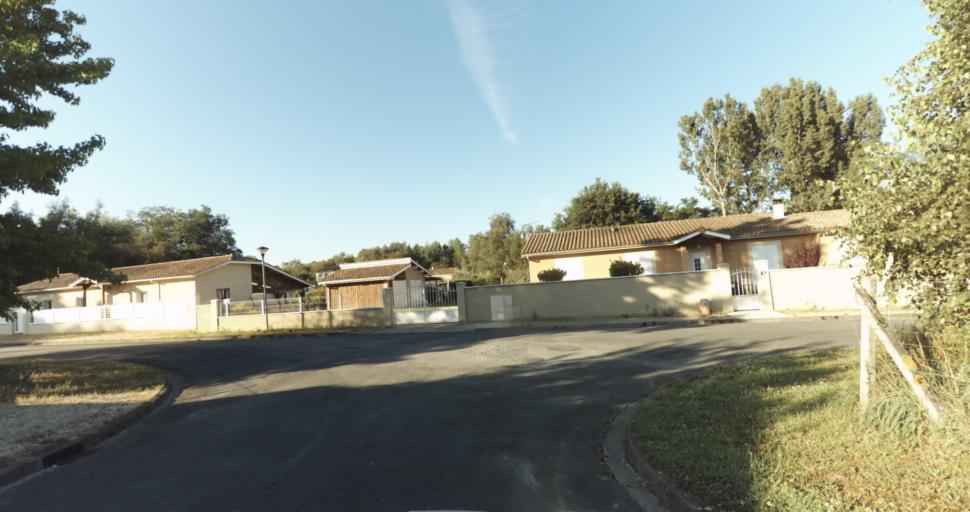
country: FR
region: Aquitaine
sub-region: Departement de la Gironde
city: Bazas
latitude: 44.4212
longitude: -0.2190
